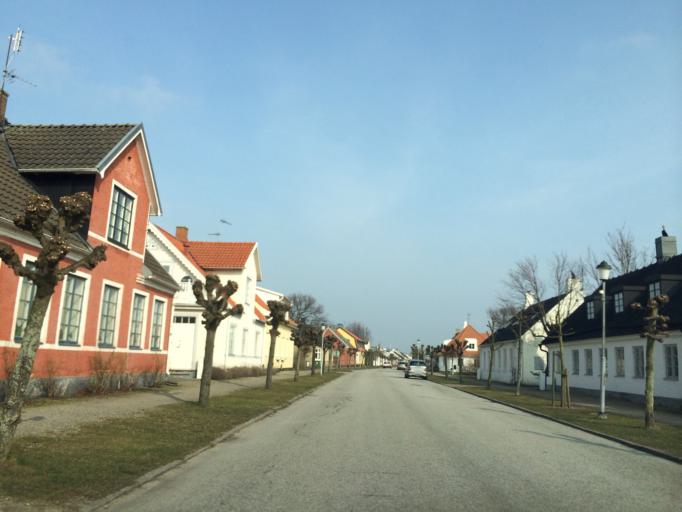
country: SE
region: Skane
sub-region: Vellinge Kommun
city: Skanor med Falsterbo
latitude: 55.4148
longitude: 12.8449
